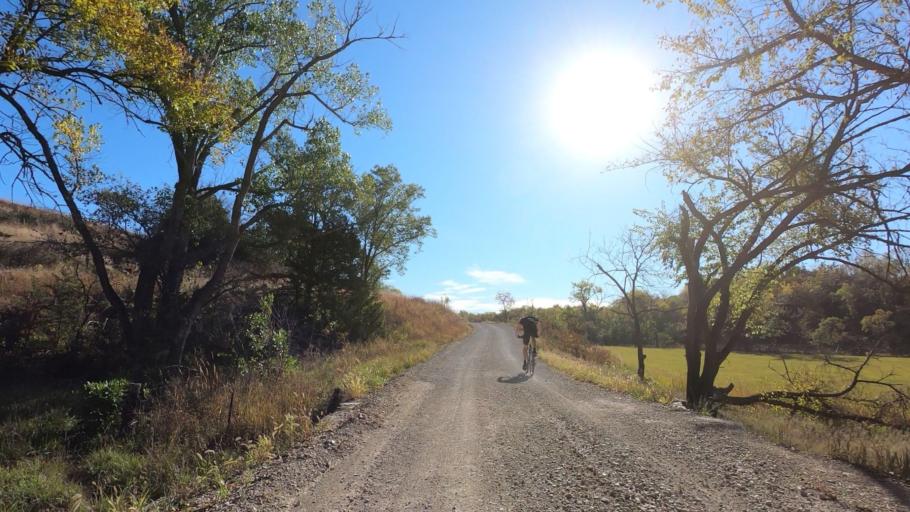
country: US
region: Kansas
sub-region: Pottawatomie County
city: Westmoreland
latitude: 39.4822
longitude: -96.5952
